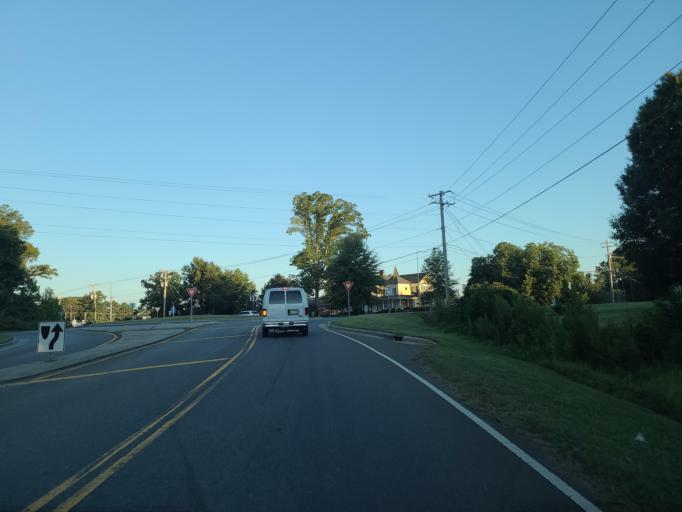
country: US
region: North Carolina
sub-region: Union County
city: Weddington
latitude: 35.0218
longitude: -80.7594
